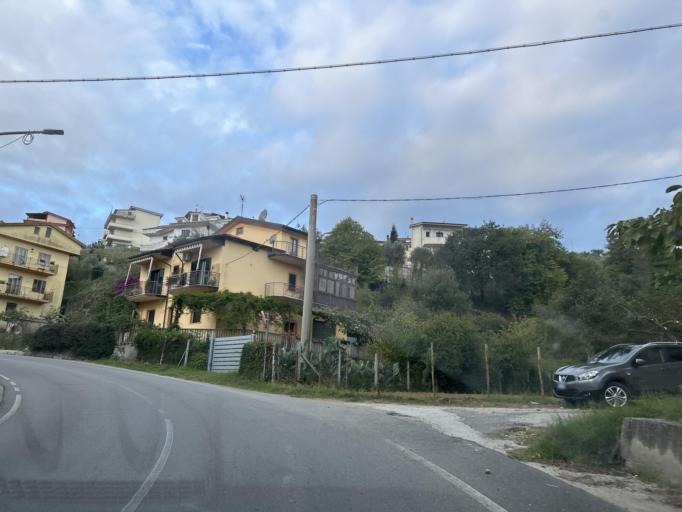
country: IT
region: Calabria
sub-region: Provincia di Catanzaro
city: Gasperina
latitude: 38.7430
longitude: 16.5068
